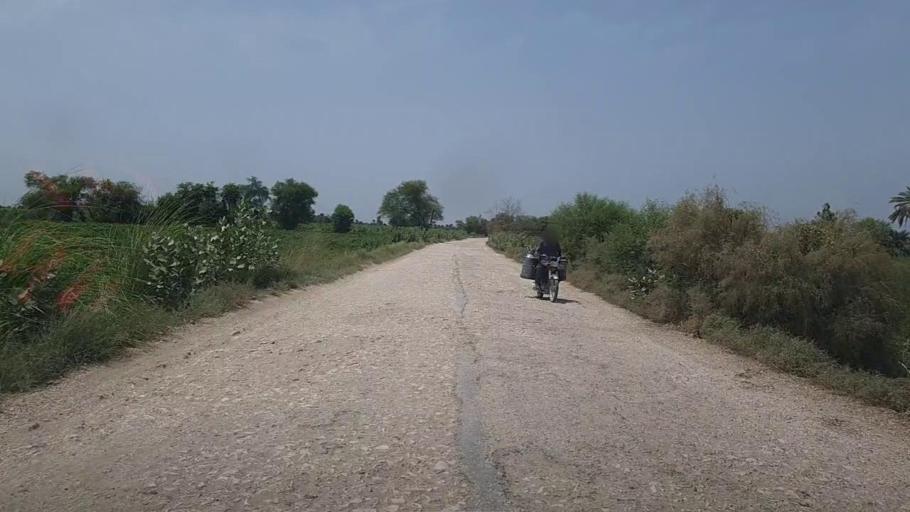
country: PK
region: Sindh
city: Pano Aqil
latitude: 27.8473
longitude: 69.1460
